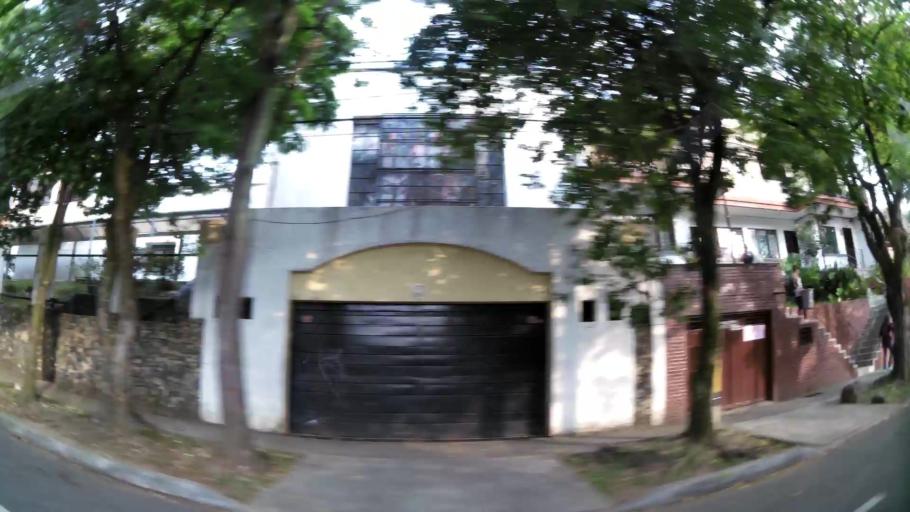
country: CO
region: Antioquia
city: Medellin
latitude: 6.2600
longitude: -75.5616
